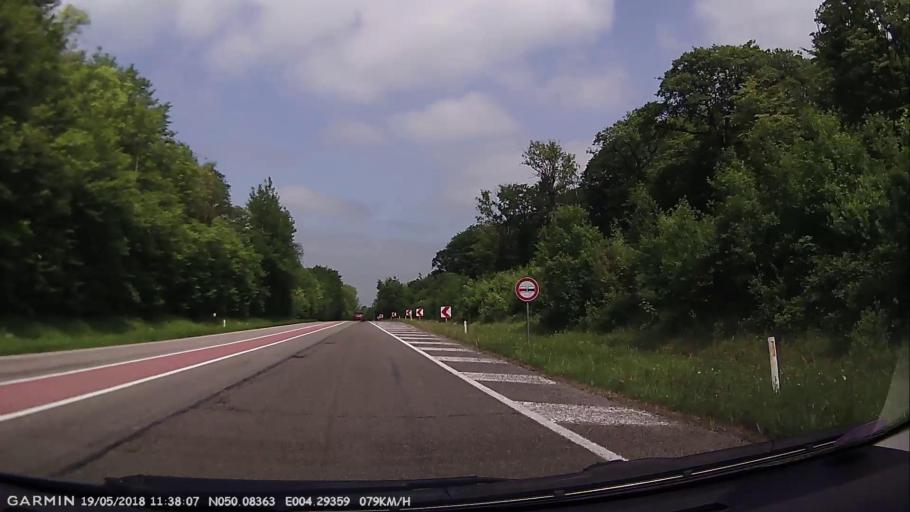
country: BE
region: Wallonia
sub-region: Province du Hainaut
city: Chimay
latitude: 50.0838
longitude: 4.2936
